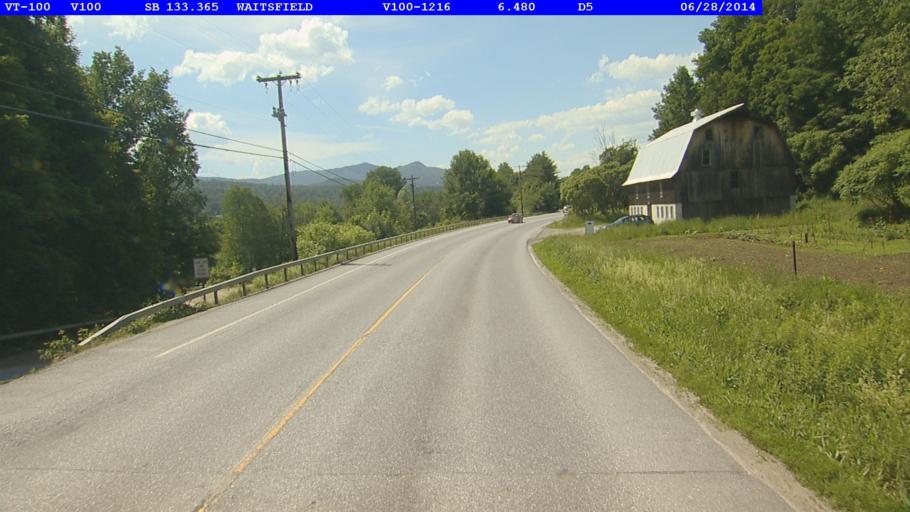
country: US
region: Vermont
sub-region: Washington County
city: Waterbury
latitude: 44.2211
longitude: -72.7899
